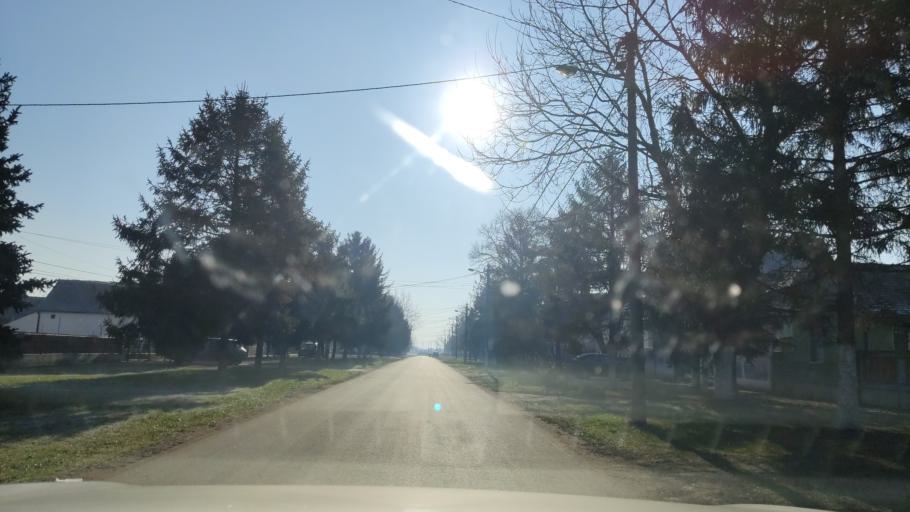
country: RS
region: Central Serbia
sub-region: Belgrade
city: Surcin
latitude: 44.7487
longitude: 20.2688
